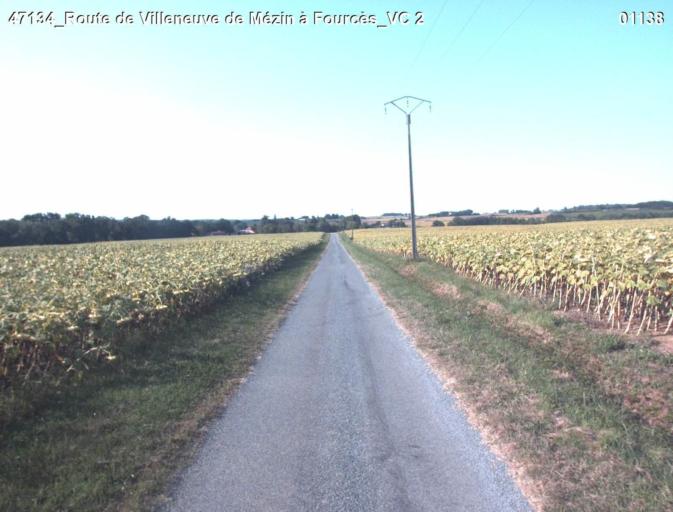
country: FR
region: Aquitaine
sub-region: Departement du Lot-et-Garonne
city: Mezin
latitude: 44.0076
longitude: 0.2486
